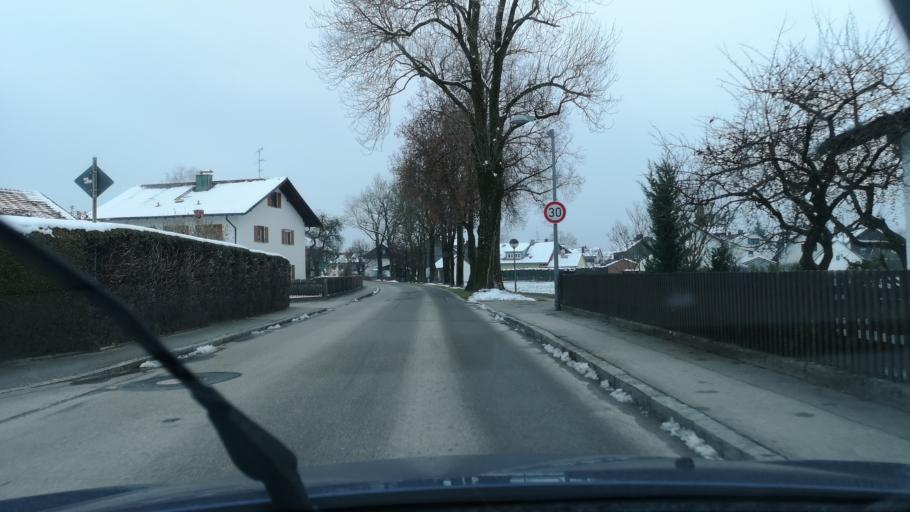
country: DE
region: Bavaria
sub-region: Upper Bavaria
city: Anzing
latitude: 48.1478
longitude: 11.8557
